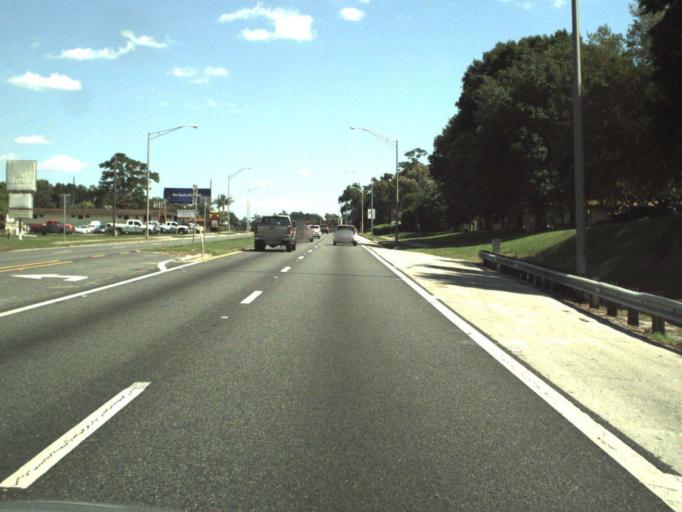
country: US
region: Florida
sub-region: Marion County
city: Ocala
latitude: 29.1601
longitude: -82.1321
